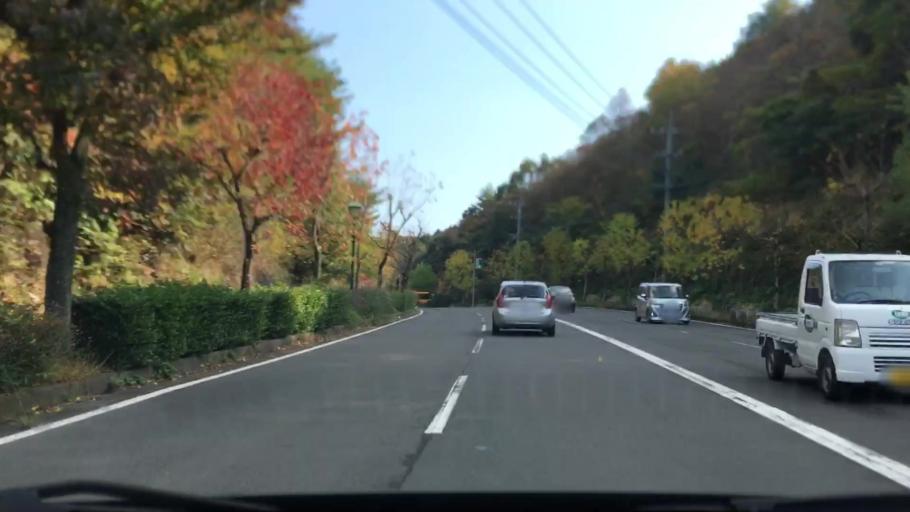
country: JP
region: Nagasaki
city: Sasebo
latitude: 32.9943
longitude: 129.7551
